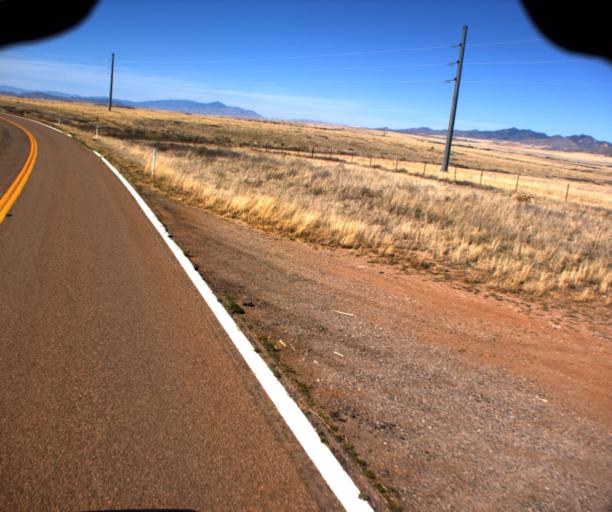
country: US
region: Arizona
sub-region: Cochise County
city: Huachuca City
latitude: 31.6184
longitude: -110.5871
